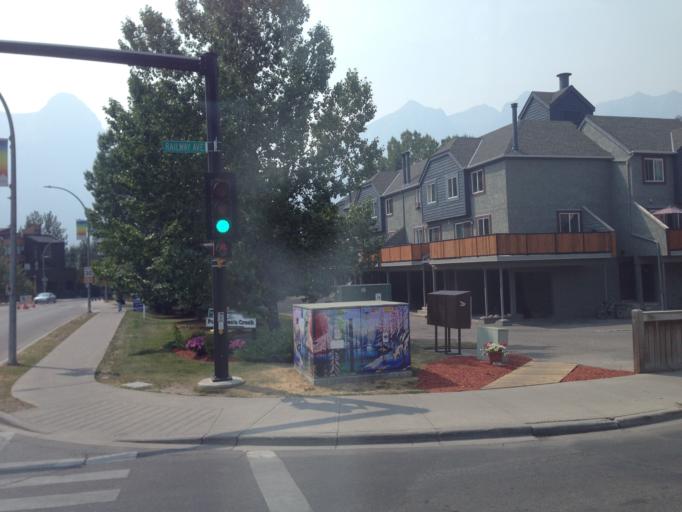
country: CA
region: Alberta
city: Canmore
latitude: 51.0912
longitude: -115.3562
